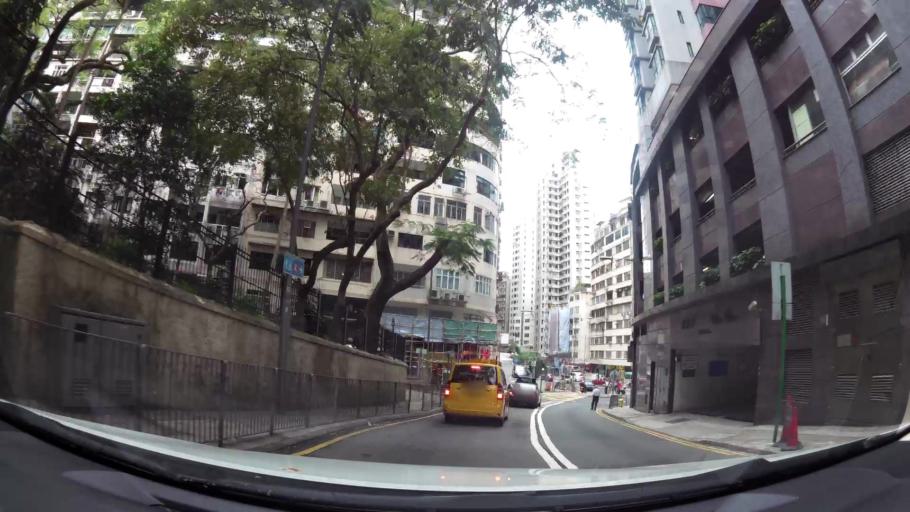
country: HK
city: Hong Kong
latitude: 22.2839
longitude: 114.1431
